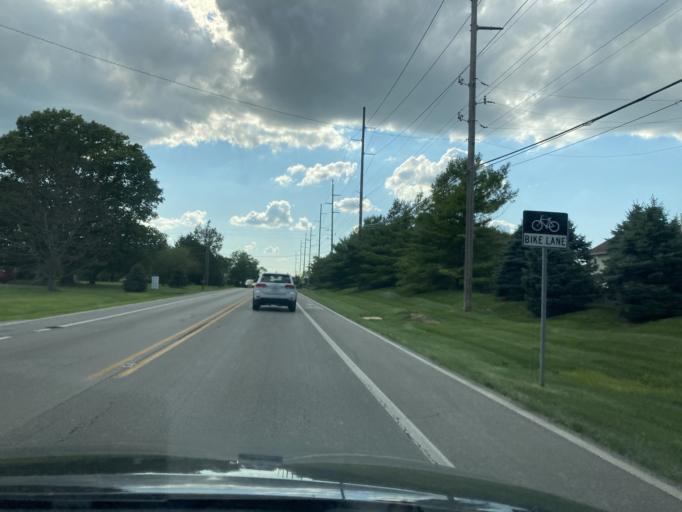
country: US
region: Indiana
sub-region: Marion County
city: Speedway
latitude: 39.8536
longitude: -86.2217
